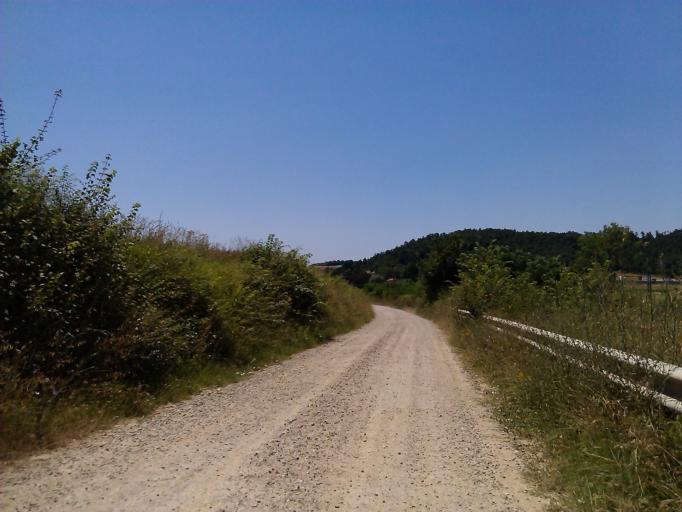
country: IT
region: Umbria
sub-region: Provincia di Terni
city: Fabro Scalo
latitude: 42.8513
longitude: 12.0409
